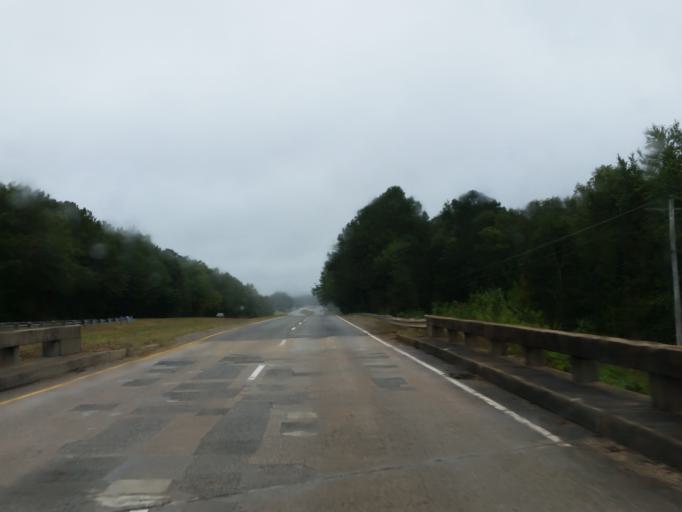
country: US
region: Georgia
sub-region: Lamar County
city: Barnesville
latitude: 33.1083
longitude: -84.1972
